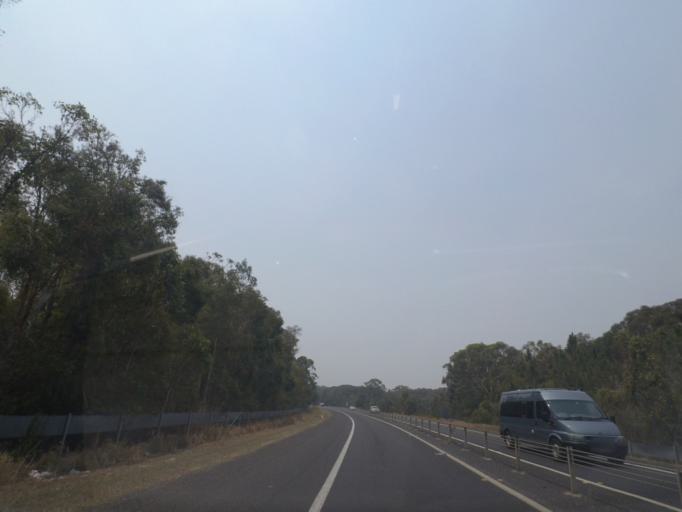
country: AU
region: New South Wales
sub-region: Ballina
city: Ballina
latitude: -28.9301
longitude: 153.4749
